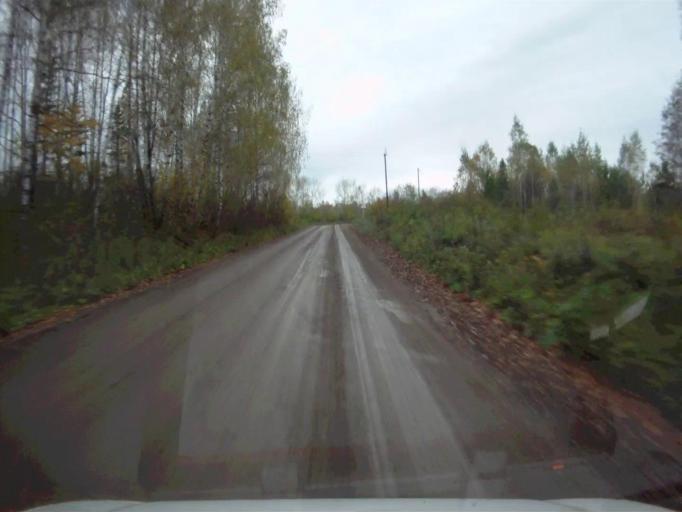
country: RU
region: Chelyabinsk
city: Nyazepetrovsk
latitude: 56.1346
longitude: 59.3073
